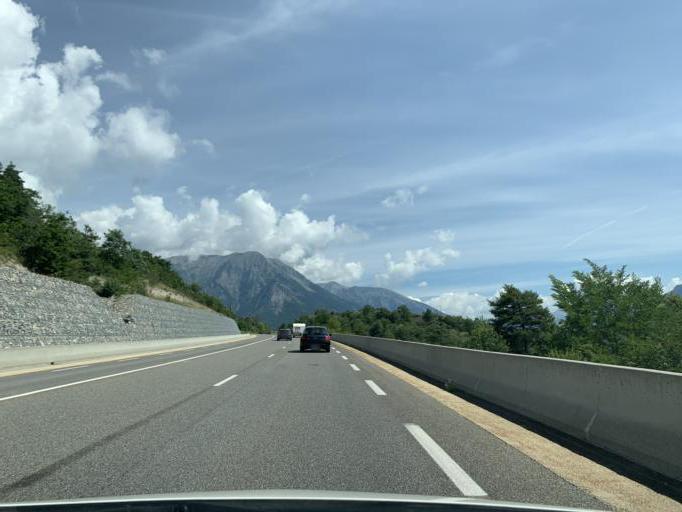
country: FR
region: Provence-Alpes-Cote d'Azur
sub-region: Departement des Hautes-Alpes
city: Embrun
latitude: 44.5735
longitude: 6.5106
